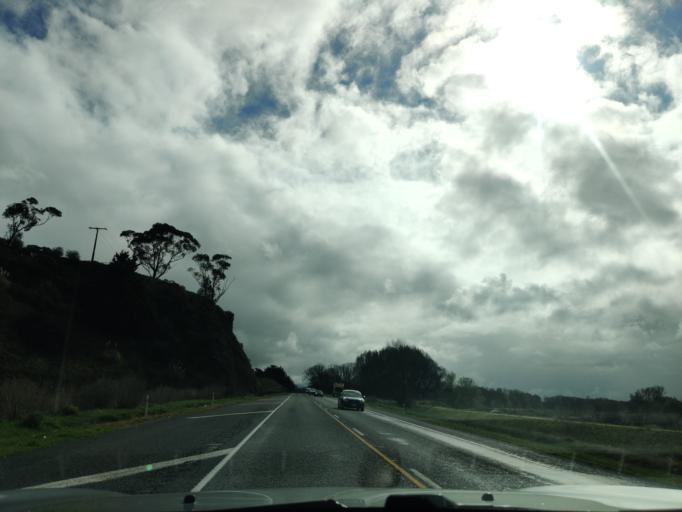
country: NZ
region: Hawke's Bay
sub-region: Hastings District
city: Hastings
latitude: -39.9780
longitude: 176.5020
